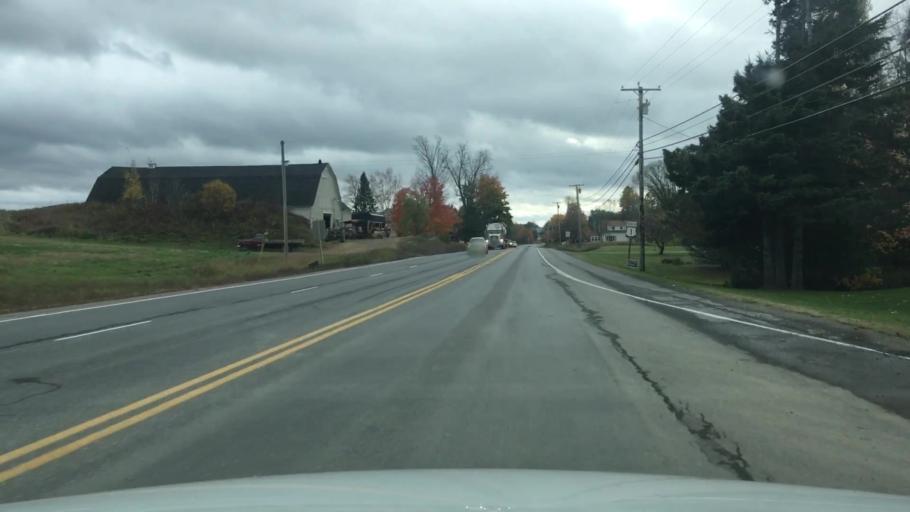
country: US
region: Maine
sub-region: Aroostook County
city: Houlton
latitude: 46.2169
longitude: -67.8410
